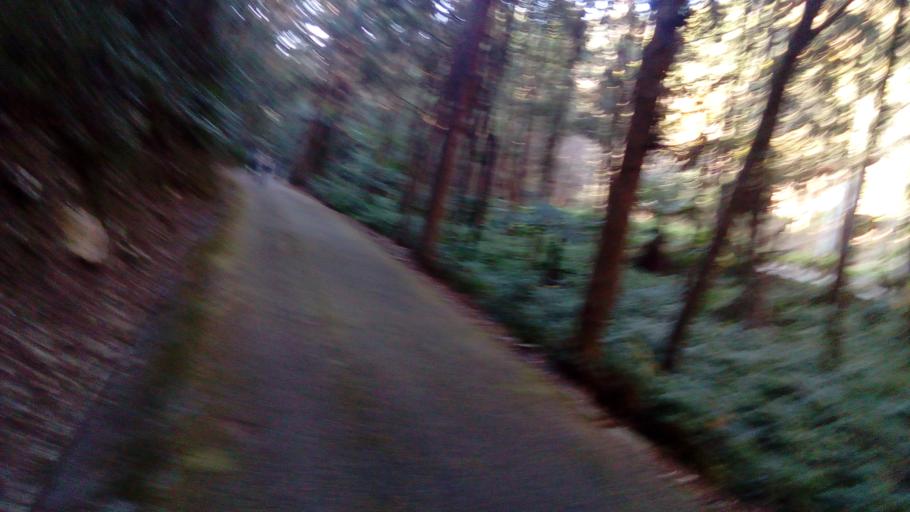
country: TW
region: Taiwan
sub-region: Nantou
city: Puli
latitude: 24.0921
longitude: 121.0340
